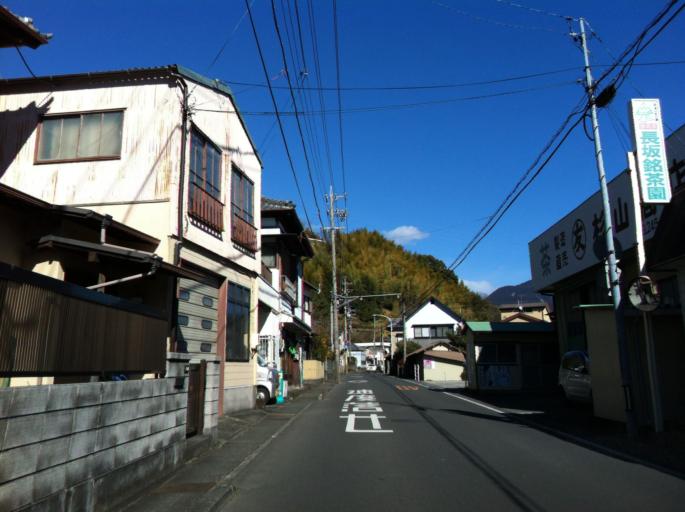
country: JP
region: Shizuoka
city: Shizuoka-shi
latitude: 35.0124
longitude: 138.3844
